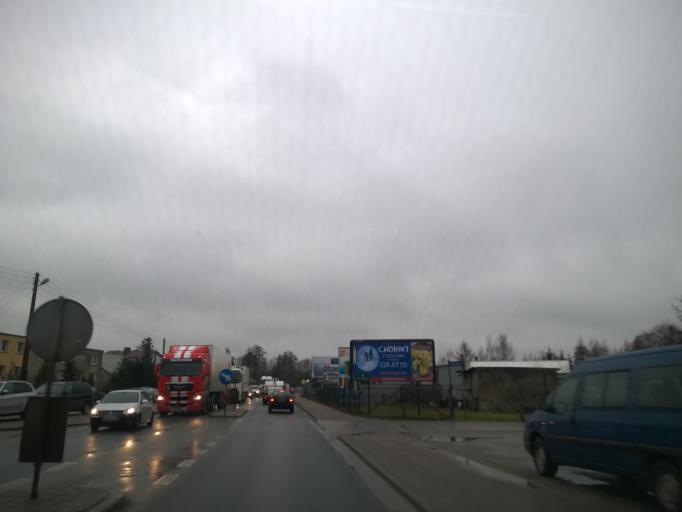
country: PL
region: Lower Silesian Voivodeship
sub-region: Powiat trzebnicki
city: Psary
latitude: 51.1844
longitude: 17.0285
